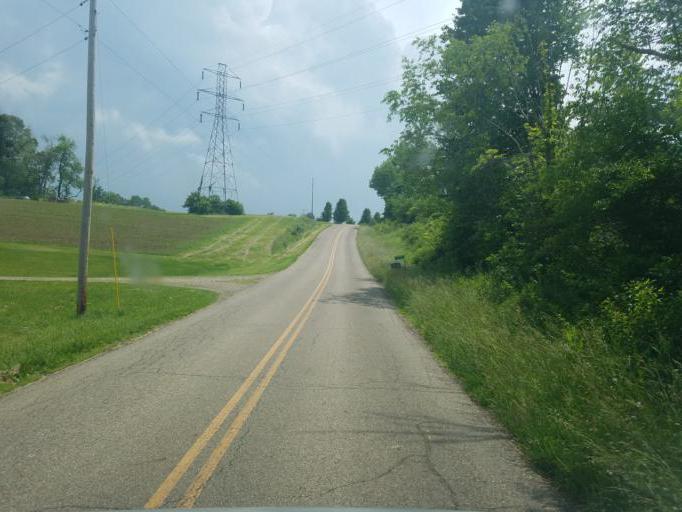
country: US
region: Ohio
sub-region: Knox County
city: Oak Hill
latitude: 40.3719
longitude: -82.2685
